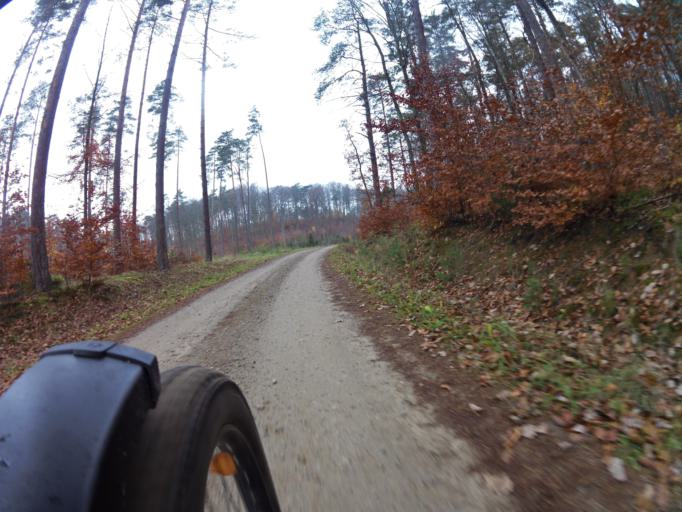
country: PL
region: Pomeranian Voivodeship
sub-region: Powiat wejherowski
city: Orle
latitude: 54.7027
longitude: 18.1459
